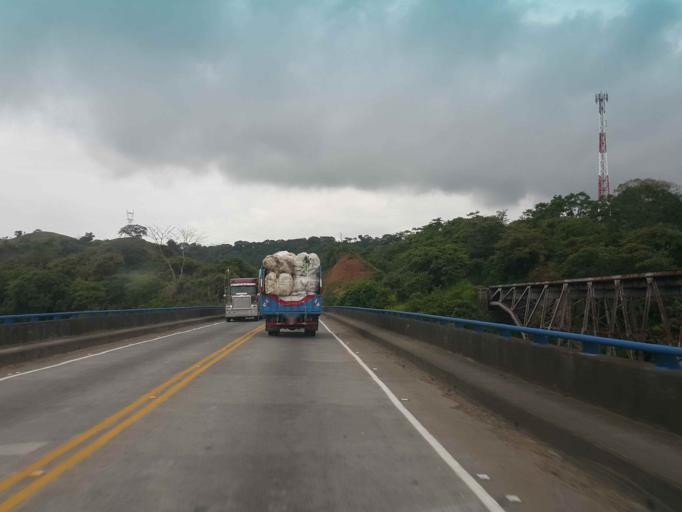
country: CR
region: Alajuela
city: Atenas
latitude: 9.9633
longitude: -84.3494
